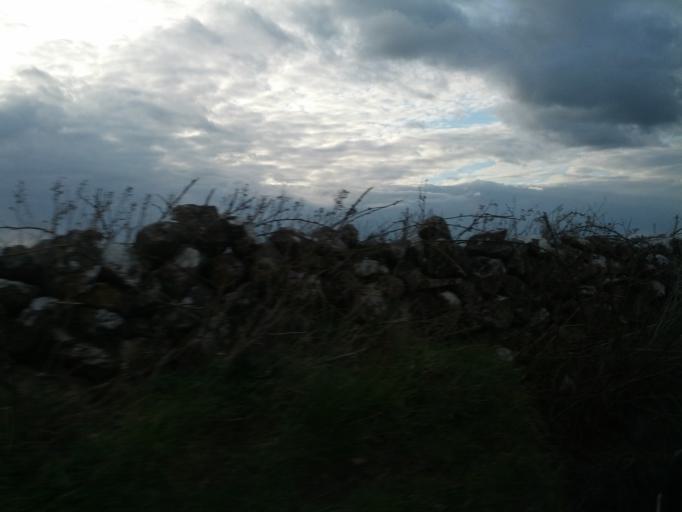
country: IE
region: Connaught
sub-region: County Galway
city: Athenry
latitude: 53.3956
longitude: -8.7471
